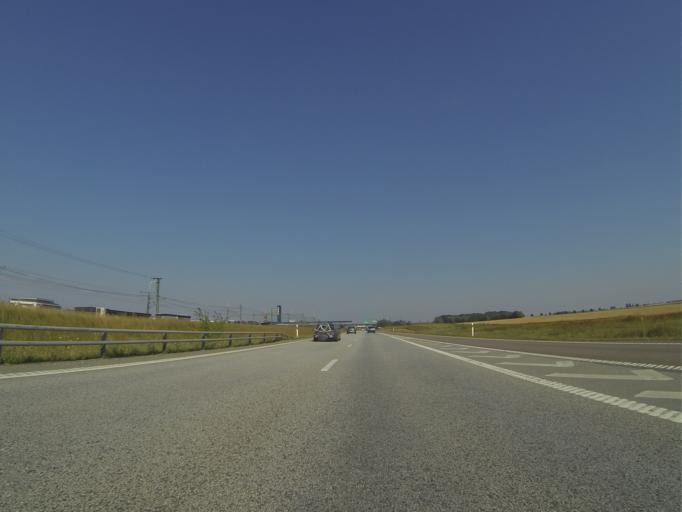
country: SE
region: Skane
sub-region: Malmo
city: Tygelsjo
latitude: 55.5465
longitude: 12.9833
